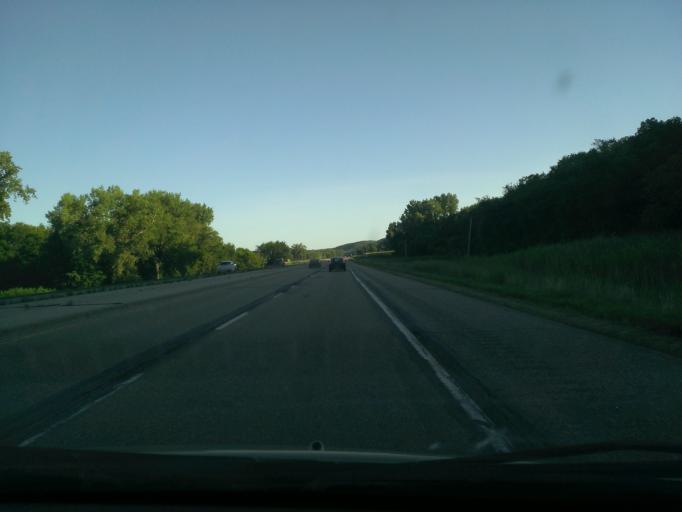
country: US
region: Minnesota
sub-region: Nicollet County
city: North Mankato
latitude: 44.2400
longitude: -94.0274
